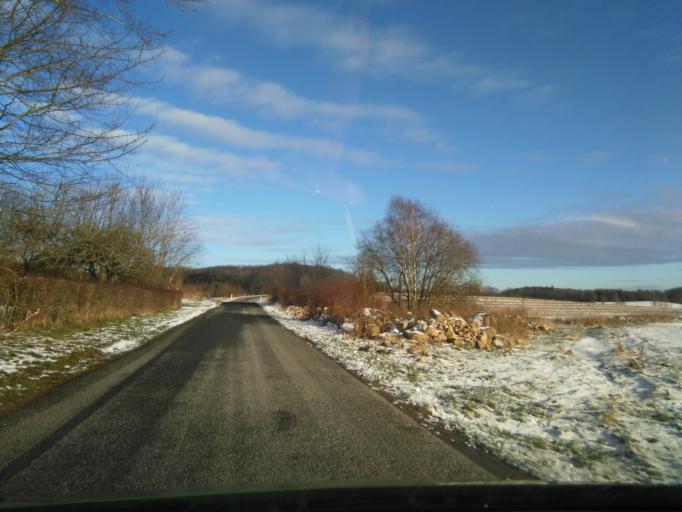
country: DK
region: Central Jutland
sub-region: Skanderborg Kommune
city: Skovby
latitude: 56.1414
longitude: 9.9568
